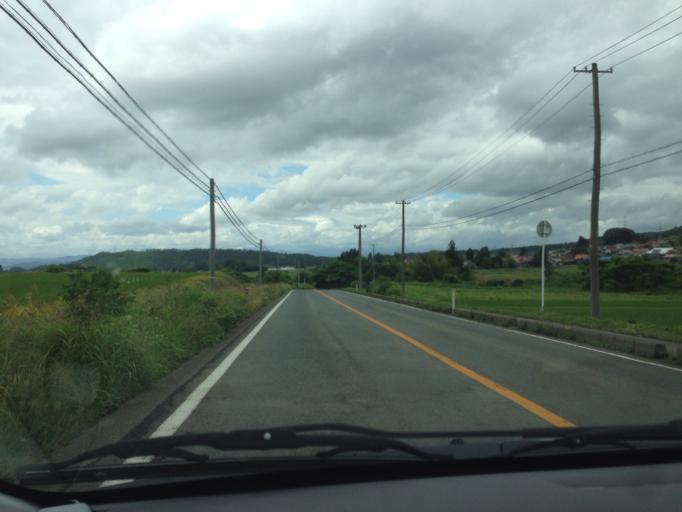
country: JP
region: Fukushima
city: Kitakata
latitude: 37.5680
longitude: 139.9654
